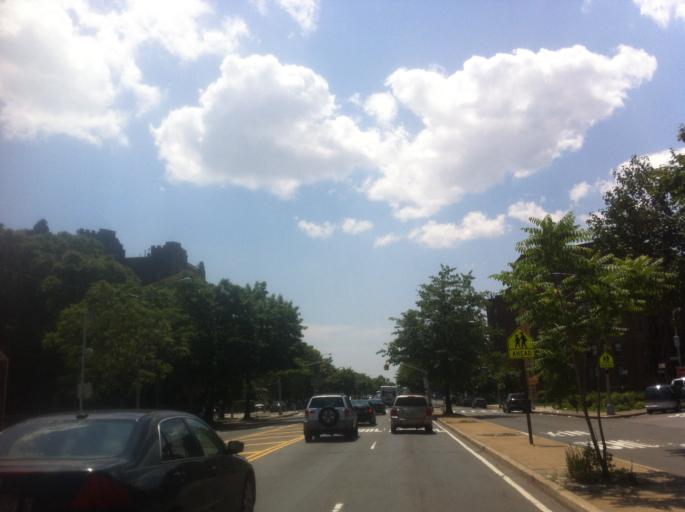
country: US
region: New York
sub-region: Kings County
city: Brooklyn
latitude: 40.6580
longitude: -73.9208
